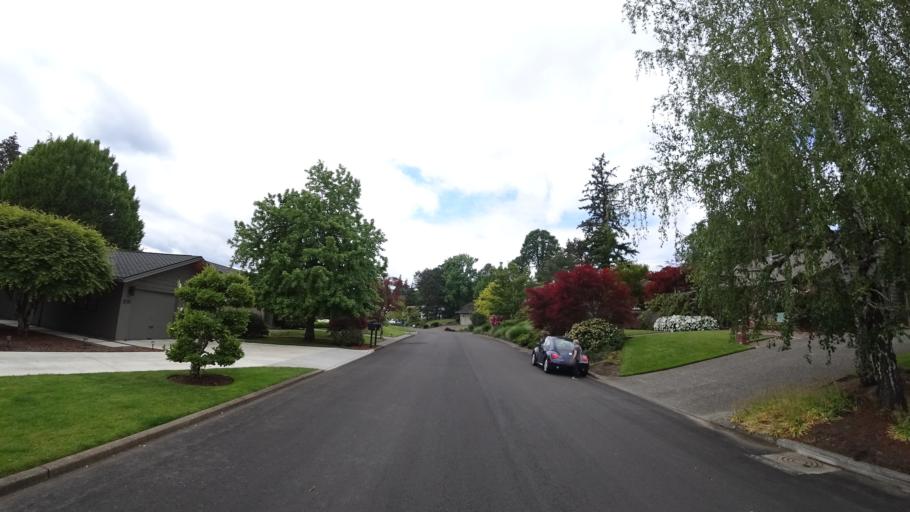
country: US
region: Oregon
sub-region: Washington County
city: Raleigh Hills
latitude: 45.4798
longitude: -122.7558
